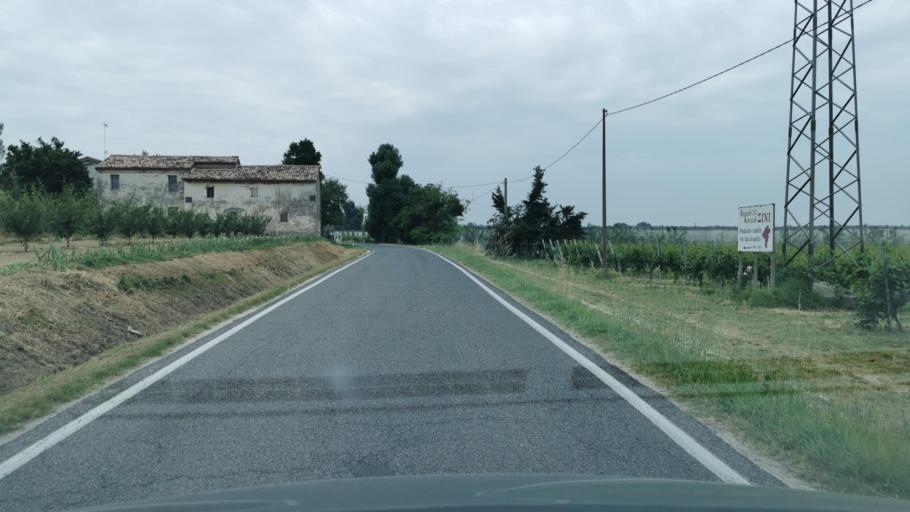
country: IT
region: Emilia-Romagna
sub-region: Provincia di Ravenna
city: Russi
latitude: 44.3978
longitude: 12.0180
